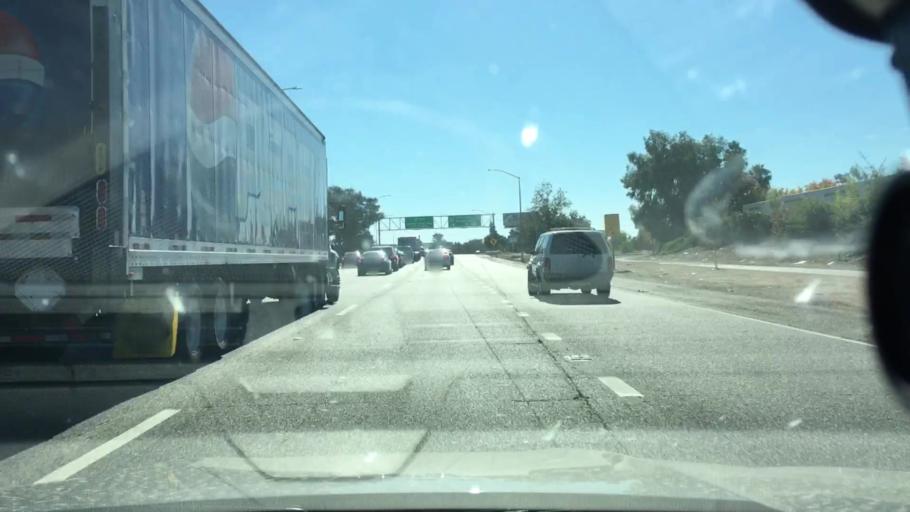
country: US
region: California
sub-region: Sacramento County
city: Arden-Arcade
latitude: 38.6056
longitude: -121.4331
